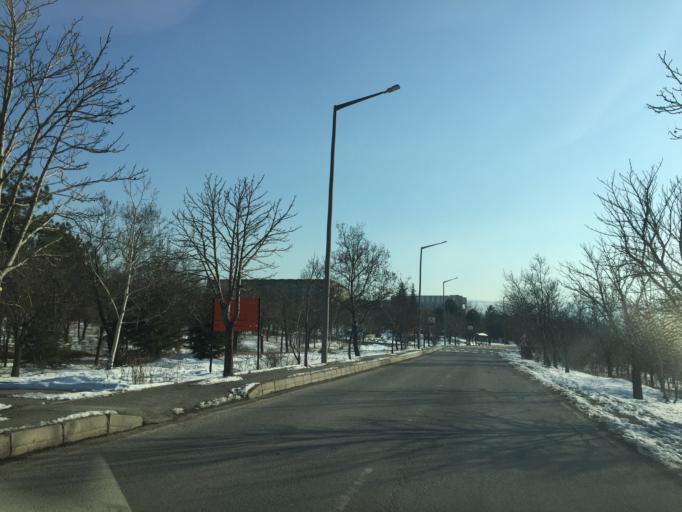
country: TR
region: Ankara
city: Ankara
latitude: 39.8993
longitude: 32.7807
